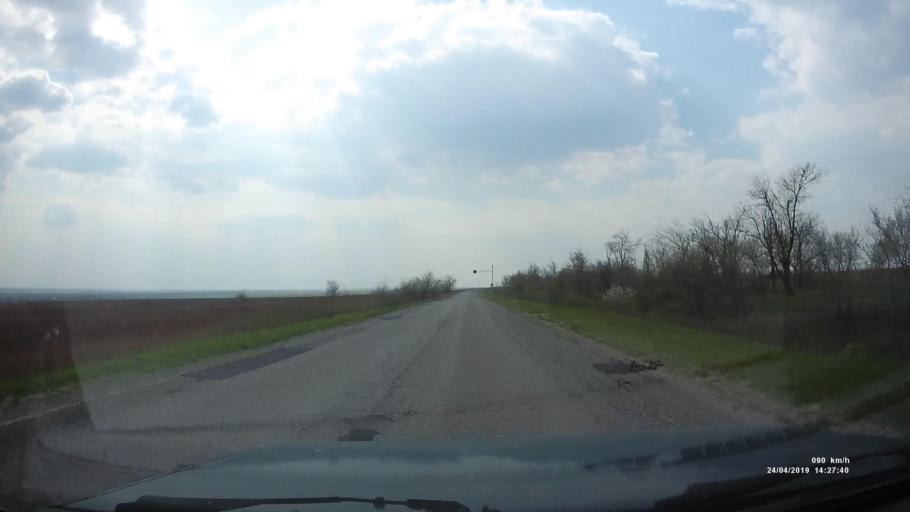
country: RU
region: Kalmykiya
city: Arshan'
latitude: 46.3339
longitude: 44.0387
